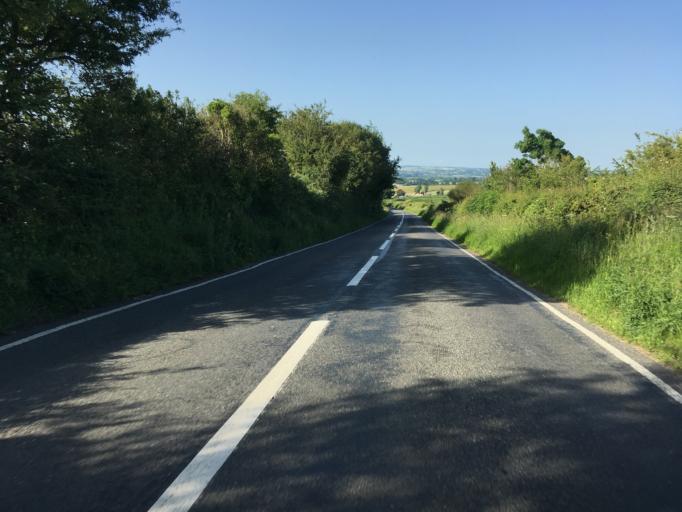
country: GB
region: England
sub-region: Oxfordshire
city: Shipton under Wychwood
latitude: 51.8443
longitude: -1.5871
